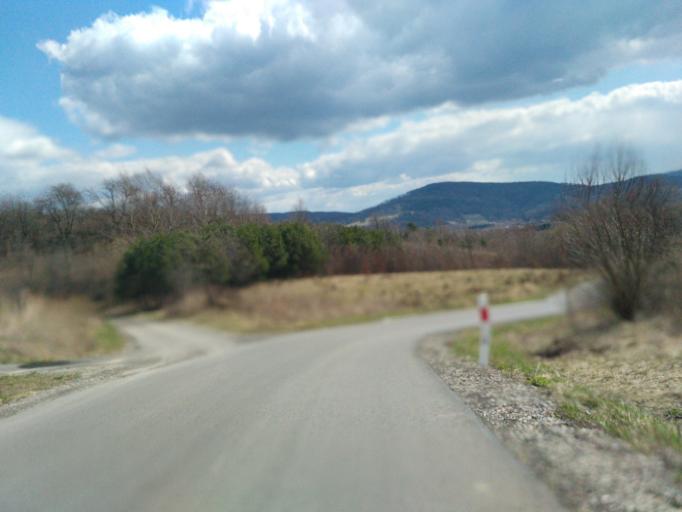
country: PL
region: Subcarpathian Voivodeship
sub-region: Powiat sanocki
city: Sanok
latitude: 49.6315
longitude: 22.2593
